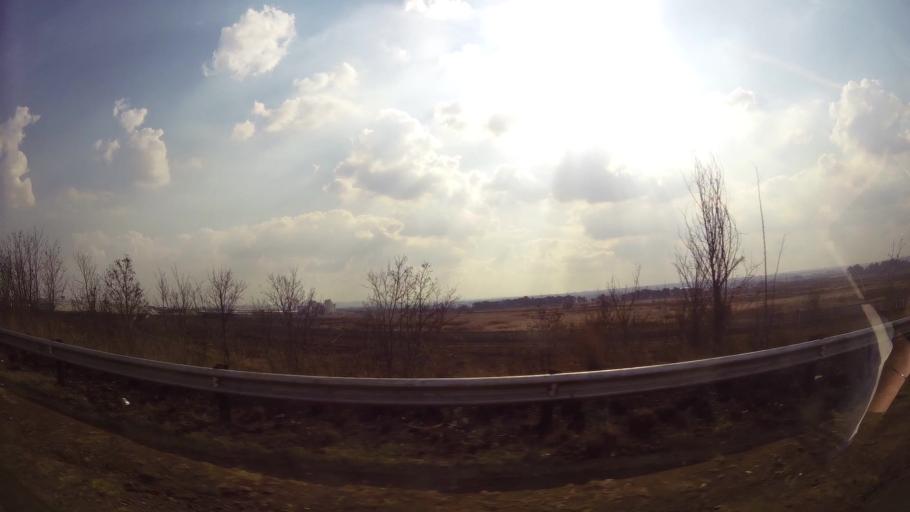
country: ZA
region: Gauteng
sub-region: Ekurhuleni Metropolitan Municipality
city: Germiston
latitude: -26.3043
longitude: 28.2099
